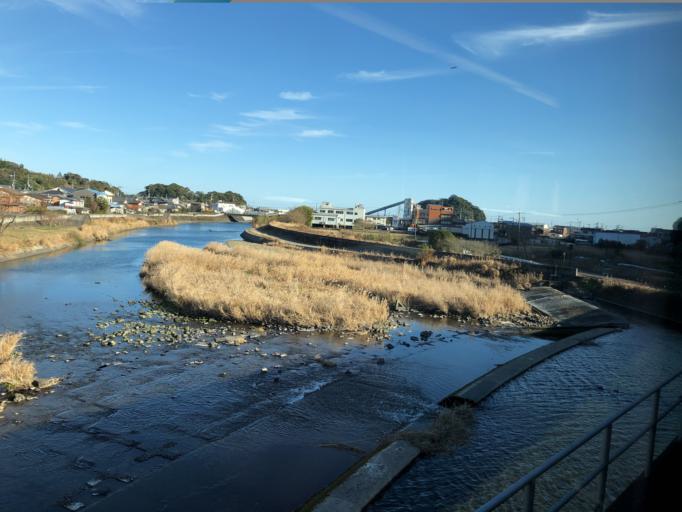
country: JP
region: Kochi
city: Nakamura
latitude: 33.0793
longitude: 133.1019
